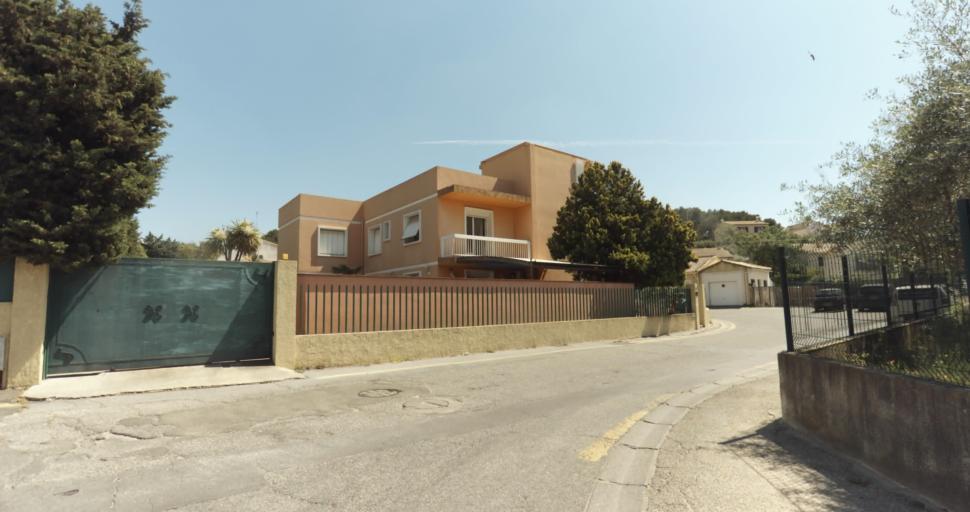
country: FR
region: Languedoc-Roussillon
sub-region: Departement du Gard
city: Nimes
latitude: 43.8209
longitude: 4.3247
